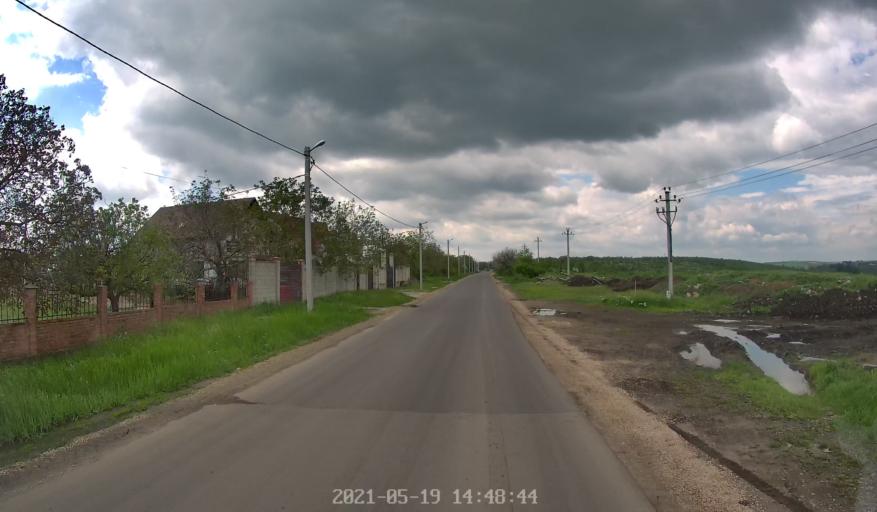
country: MD
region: Chisinau
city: Stauceni
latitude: 47.0461
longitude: 28.9582
